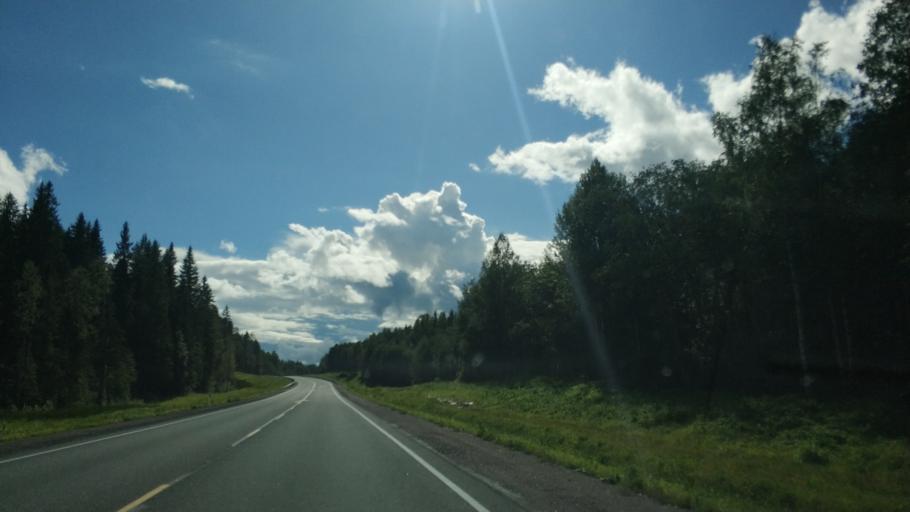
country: RU
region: Republic of Karelia
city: Ruskeala
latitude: 61.8544
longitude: 30.6512
